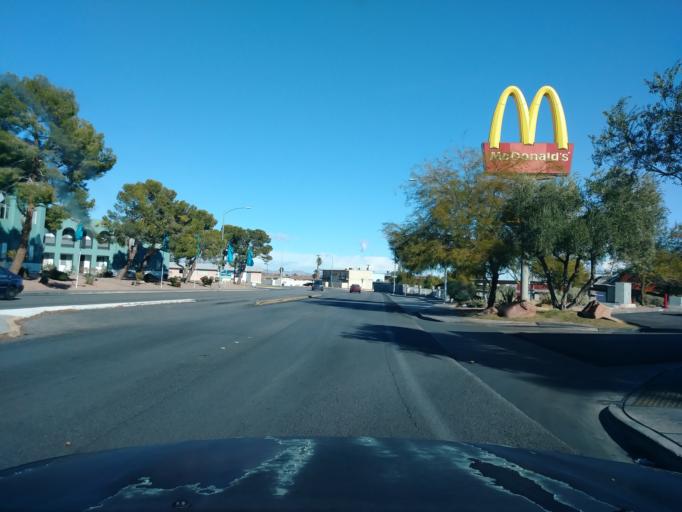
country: US
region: Nevada
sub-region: Clark County
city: Spring Valley
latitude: 36.1599
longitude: -115.2344
